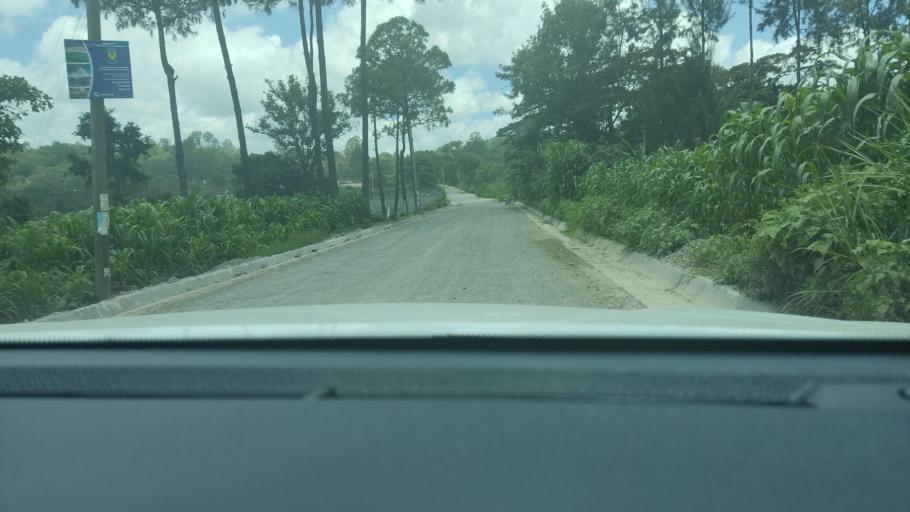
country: GT
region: Chimaltenango
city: San Martin Jilotepeque
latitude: 14.7980
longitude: -90.8150
